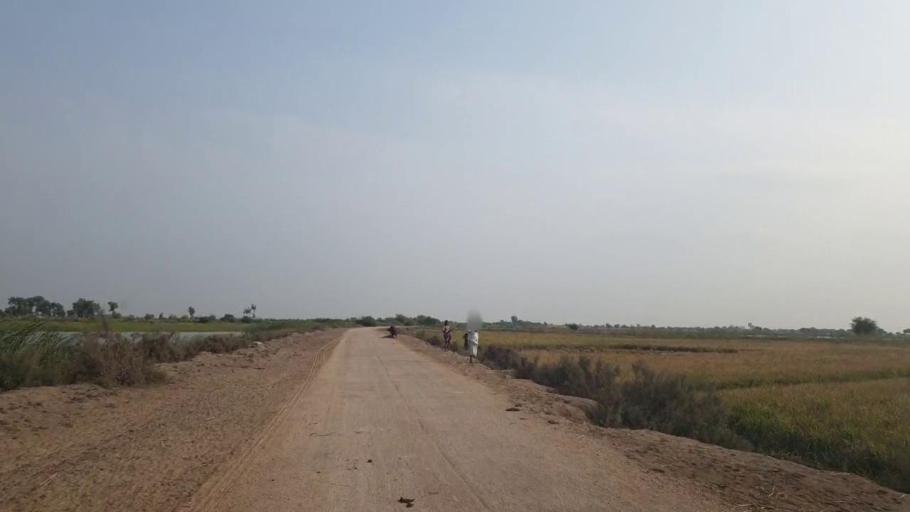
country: PK
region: Sindh
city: Badin
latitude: 24.6048
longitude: 68.6937
